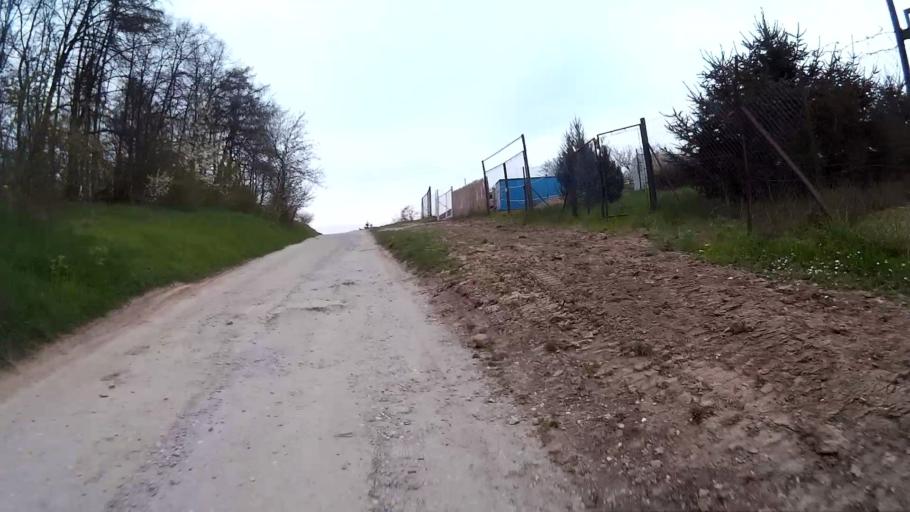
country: CZ
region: South Moravian
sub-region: Mesto Brno
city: Mokra Hora
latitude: 49.2291
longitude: 16.5501
